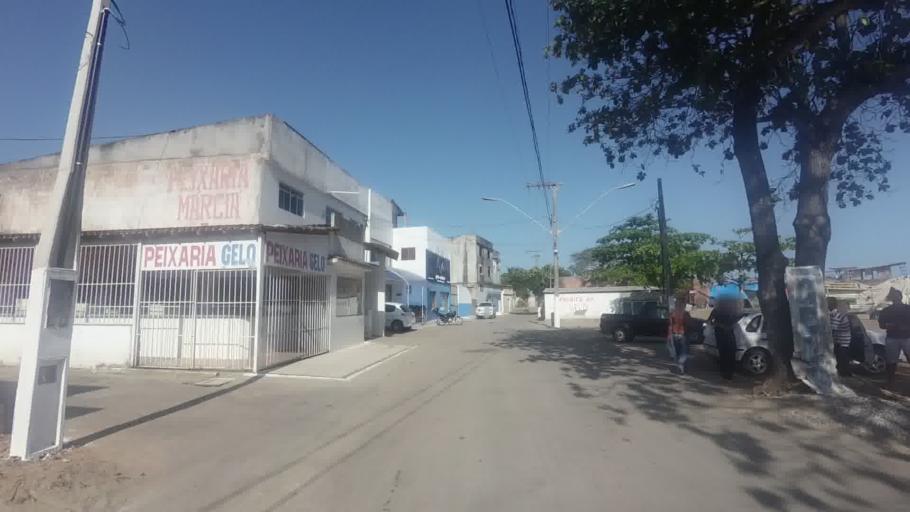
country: BR
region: Espirito Santo
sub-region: Piuma
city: Piuma
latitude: -20.8909
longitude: -40.7692
